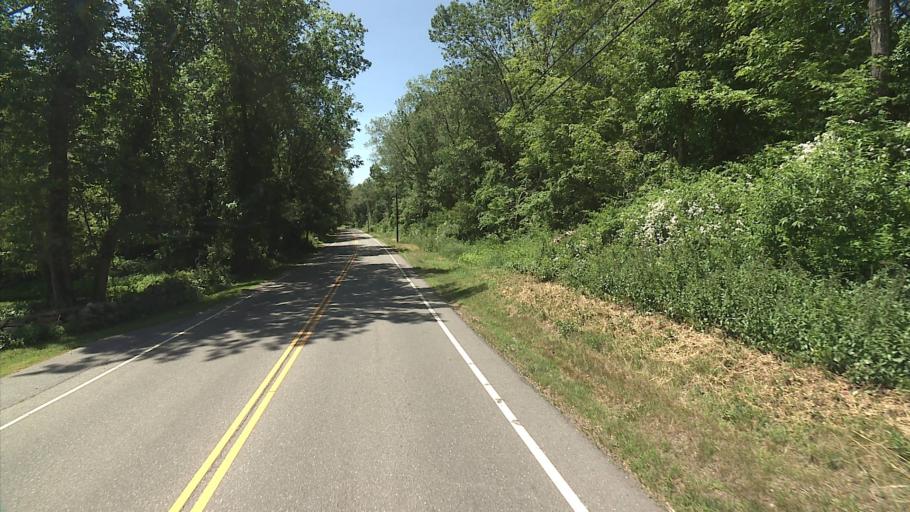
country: US
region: Rhode Island
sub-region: Washington County
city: Hopkinton
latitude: 41.4927
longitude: -71.8328
